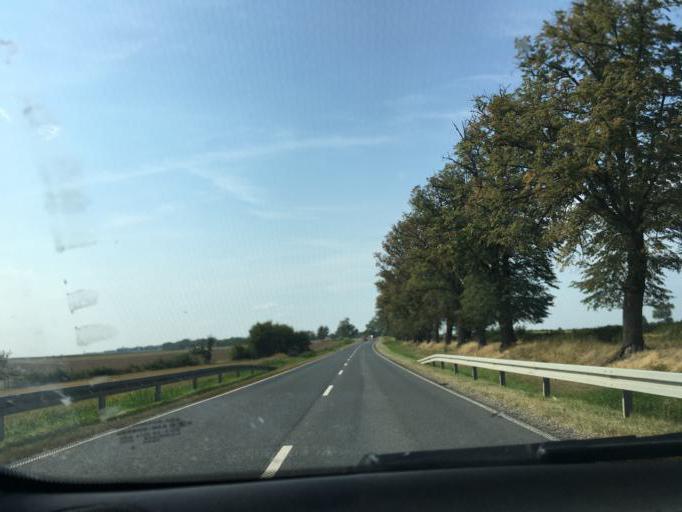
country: PL
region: Opole Voivodeship
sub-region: Powiat prudnicki
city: Laka Prudnicka
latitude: 50.4159
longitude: 17.4878
